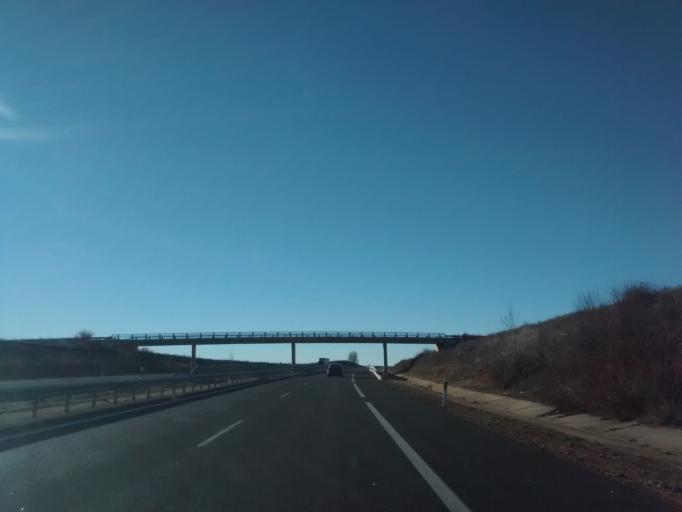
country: ES
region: Castille and Leon
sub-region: Provincia de Palencia
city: Espinosa de Villagonzalo
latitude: 42.4643
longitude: -4.3844
